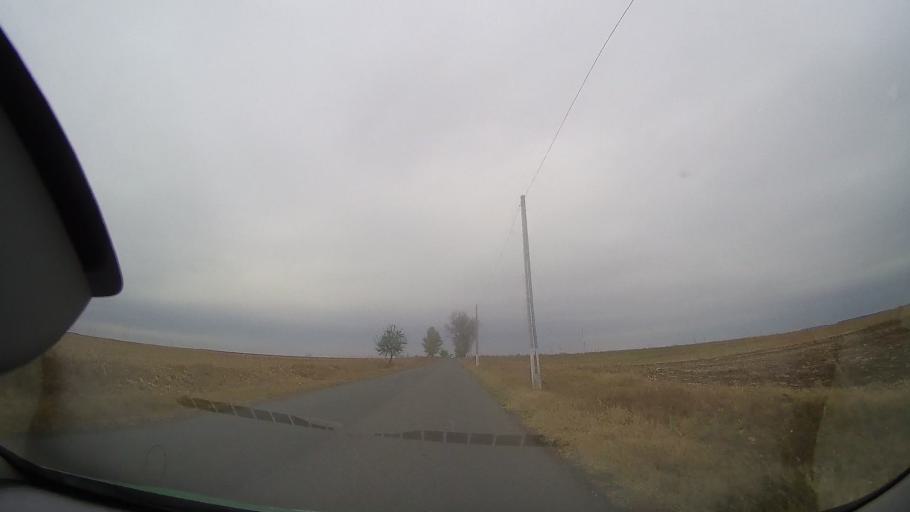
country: RO
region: Braila
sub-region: Comuna Budesti
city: Tataru
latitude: 44.8632
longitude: 27.4258
